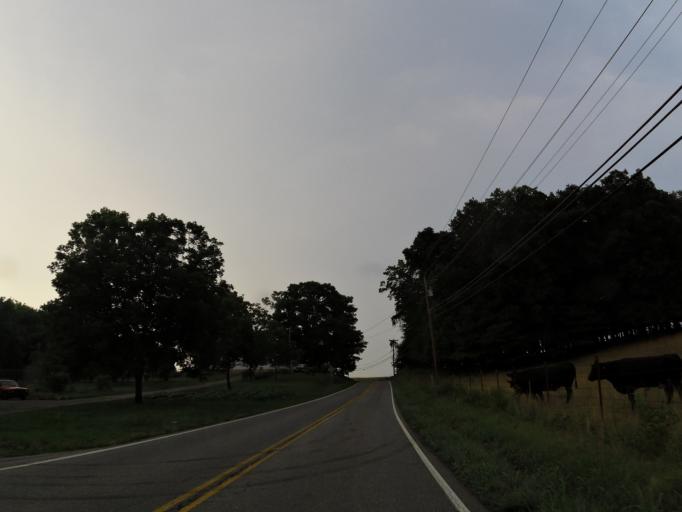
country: US
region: Tennessee
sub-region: Blount County
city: Wildwood
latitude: 35.7967
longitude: -83.8559
